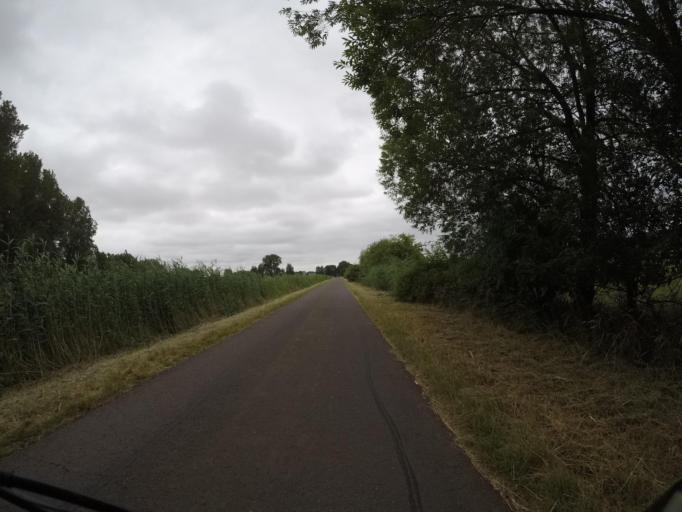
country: DE
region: Lower Saxony
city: Hitzacker
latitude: 53.1583
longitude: 11.0868
